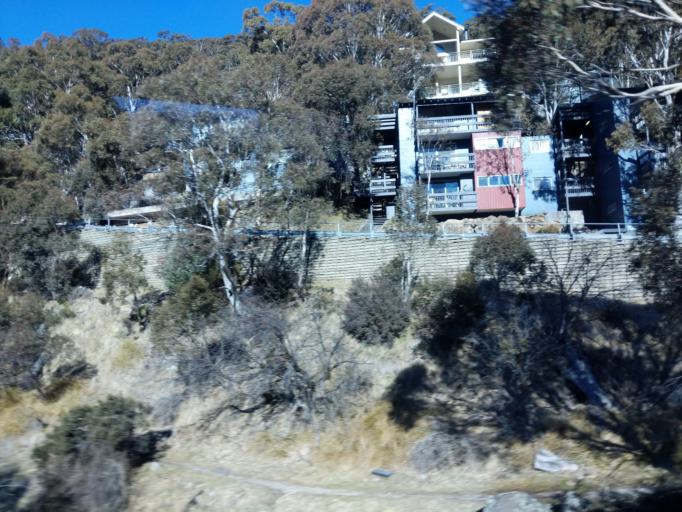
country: AU
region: New South Wales
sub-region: Snowy River
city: Jindabyne
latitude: -36.5029
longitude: 148.3087
